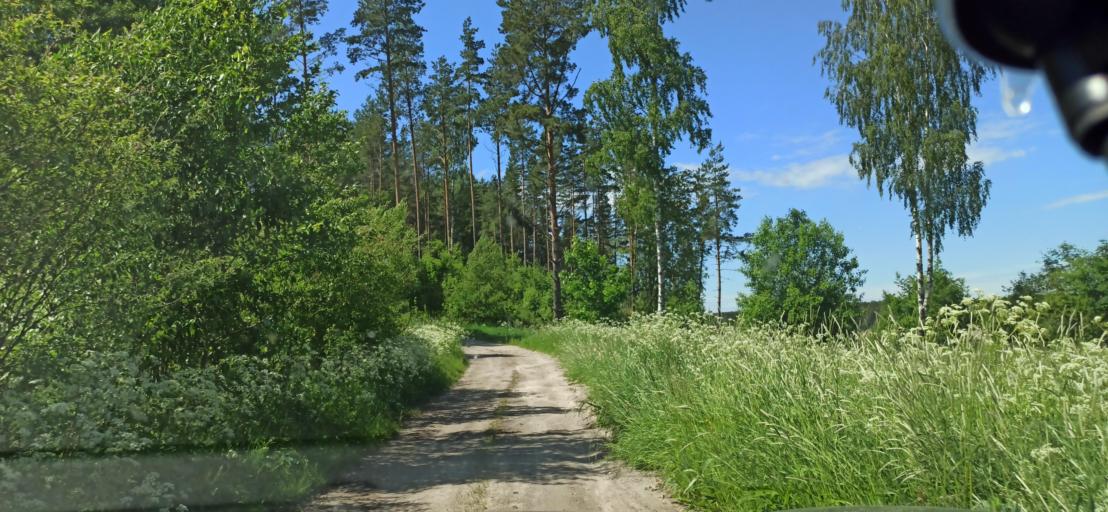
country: FI
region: Varsinais-Suomi
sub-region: Turku
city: Sauvo
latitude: 60.3833
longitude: 22.6258
